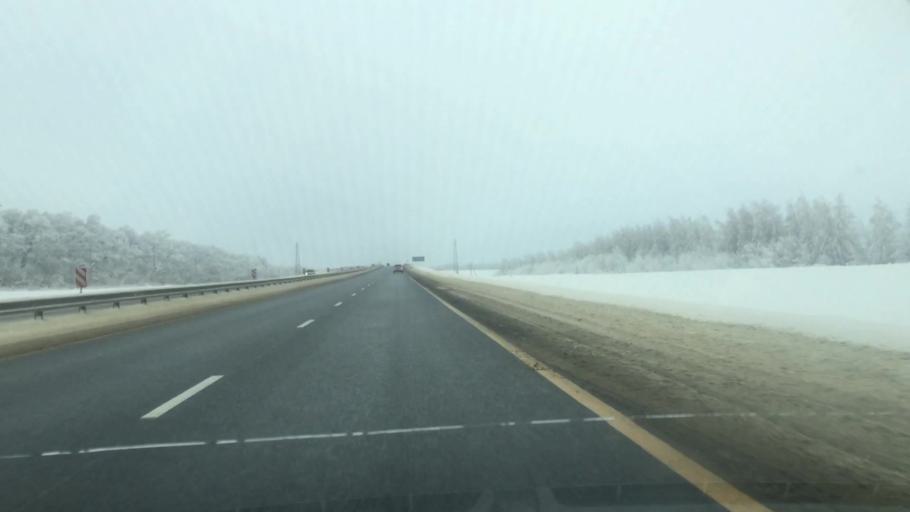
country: RU
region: Lipetsk
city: Zadonsk
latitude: 52.5098
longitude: 38.7557
